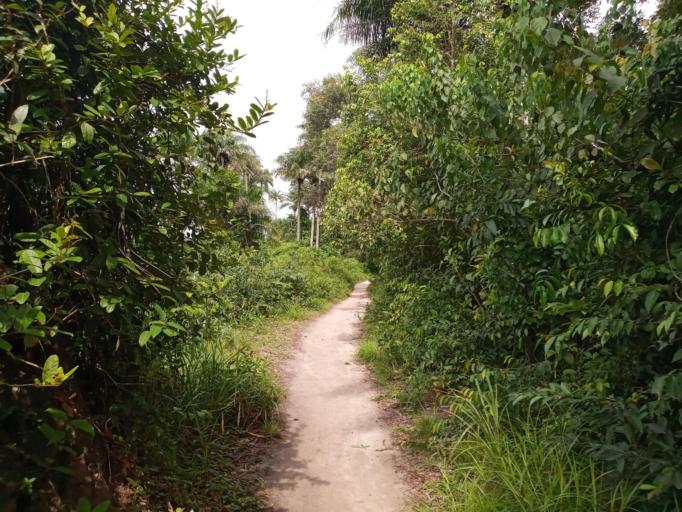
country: SL
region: Southern Province
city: Bonthe
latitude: 7.5160
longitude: -12.5444
